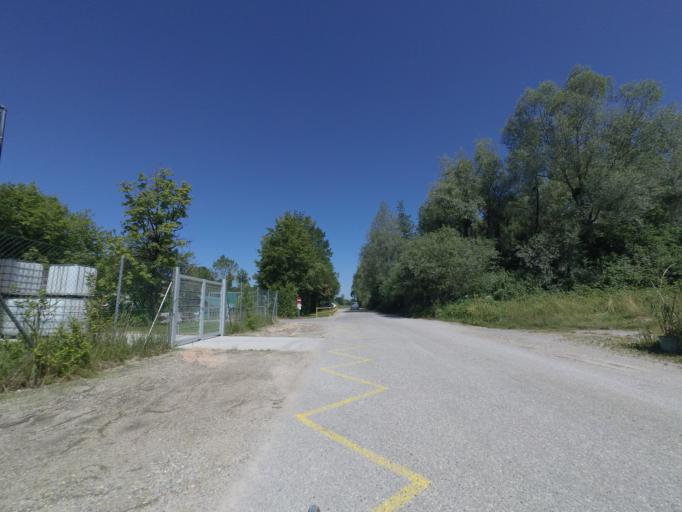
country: AT
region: Salzburg
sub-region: Politischer Bezirk Salzburg-Umgebung
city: Anif
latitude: 47.7316
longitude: 13.0691
